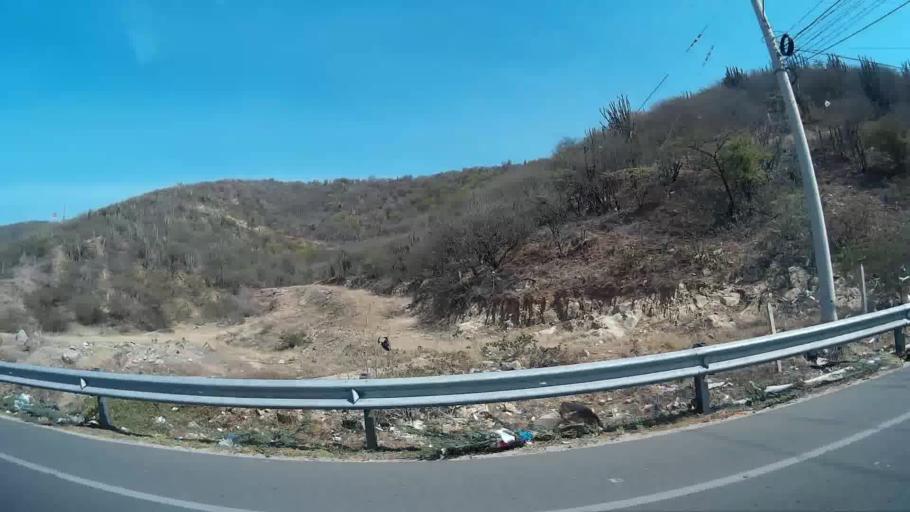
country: CO
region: Magdalena
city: Santa Marta
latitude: 11.1813
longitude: -74.2269
